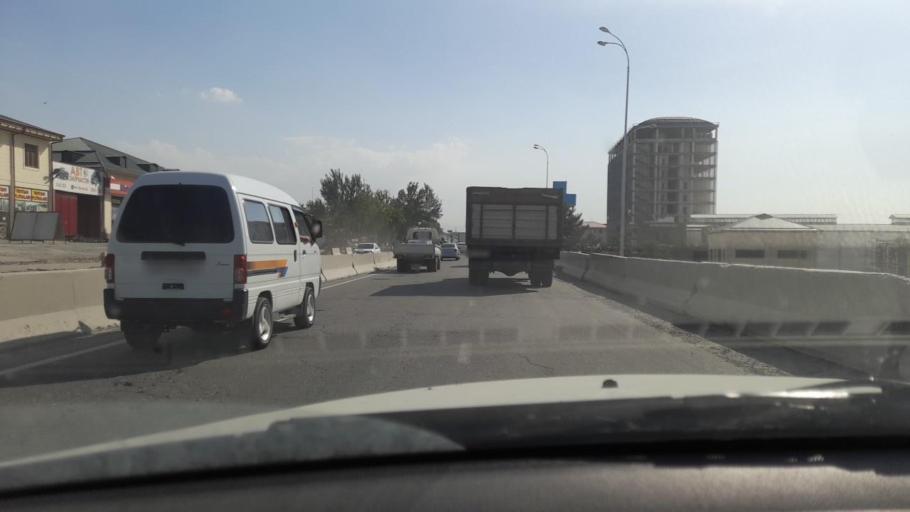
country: UZ
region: Samarqand
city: Samarqand
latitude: 39.6892
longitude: 67.0102
